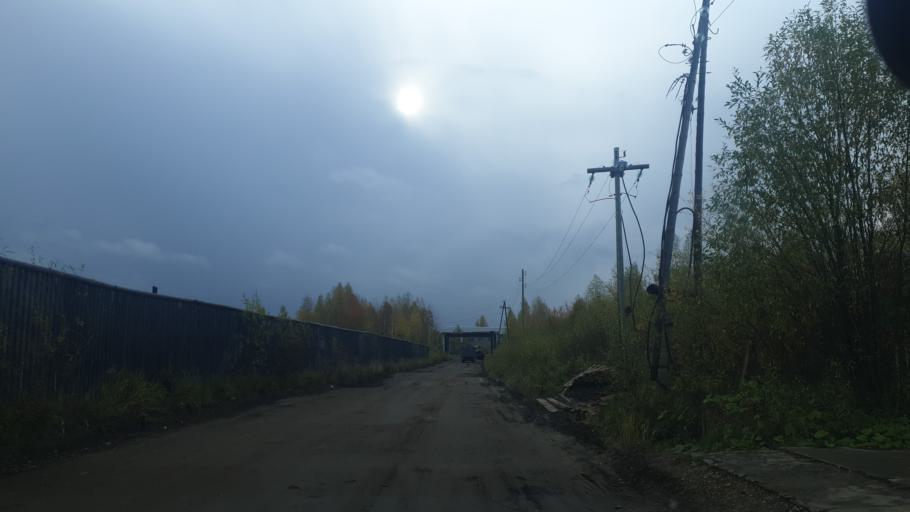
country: RU
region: Komi Republic
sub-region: Syktyvdinskiy Rayon
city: Syktyvkar
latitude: 61.7258
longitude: 50.7479
